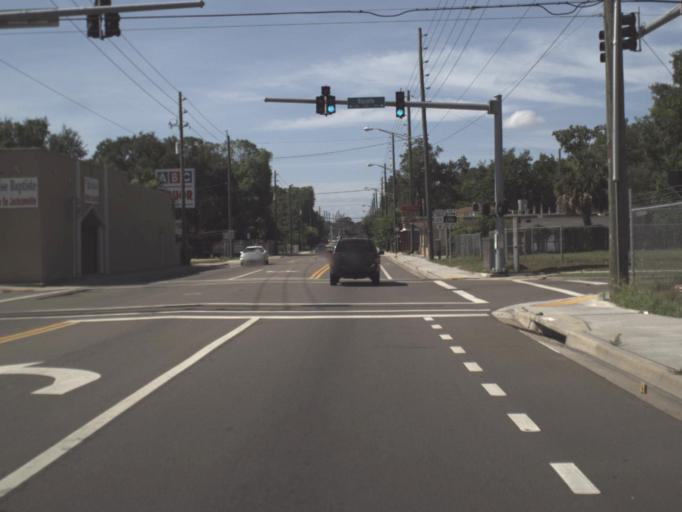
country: US
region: Florida
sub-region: Duval County
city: Jacksonville
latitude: 30.3194
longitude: -81.7055
